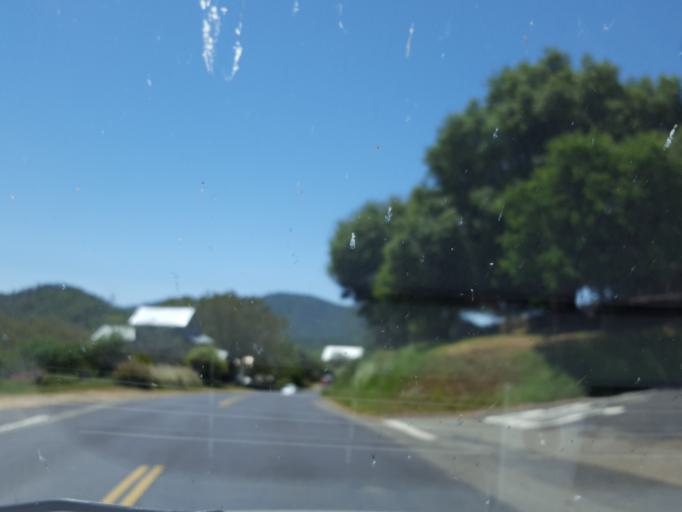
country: US
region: California
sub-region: Tuolumne County
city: Tuolumne City
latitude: 37.7144
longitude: -120.1938
